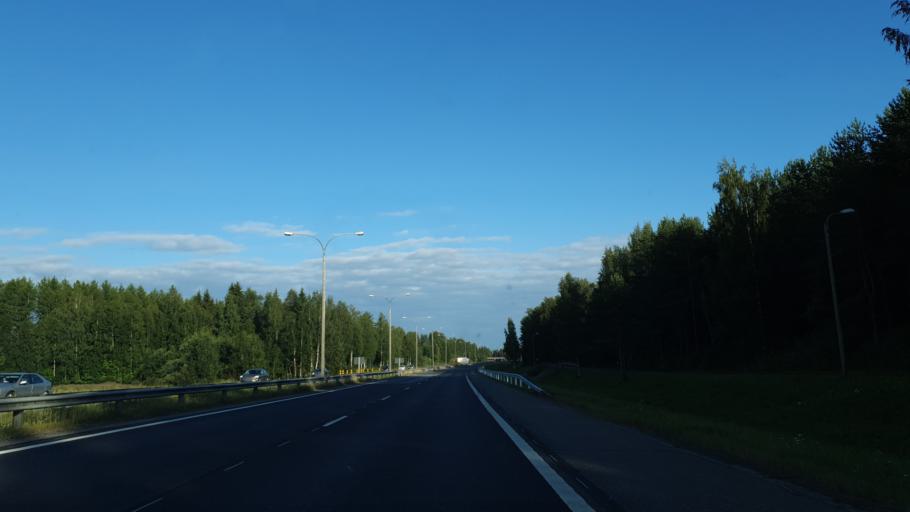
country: FI
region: North Karelia
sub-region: Joensuu
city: Joensuu
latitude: 62.6219
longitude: 29.7203
